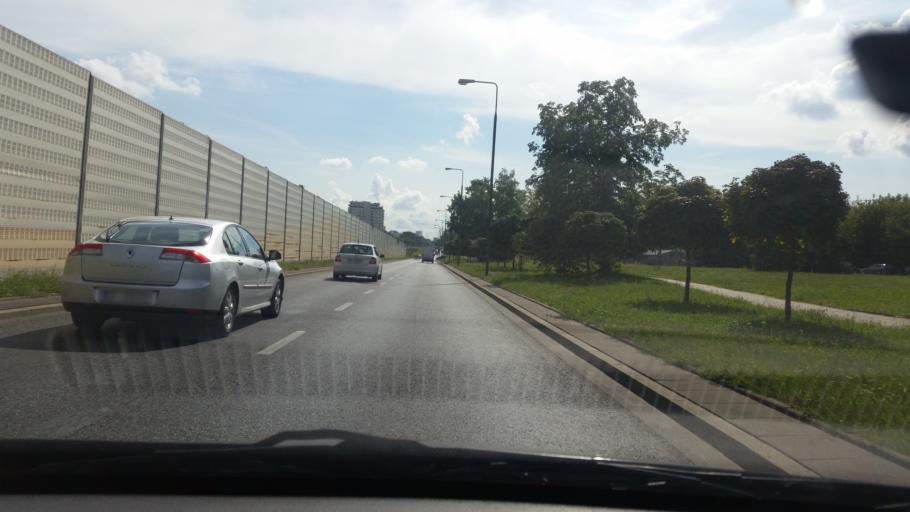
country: PL
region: Masovian Voivodeship
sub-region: Warszawa
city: Bielany
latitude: 52.2648
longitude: 20.9465
